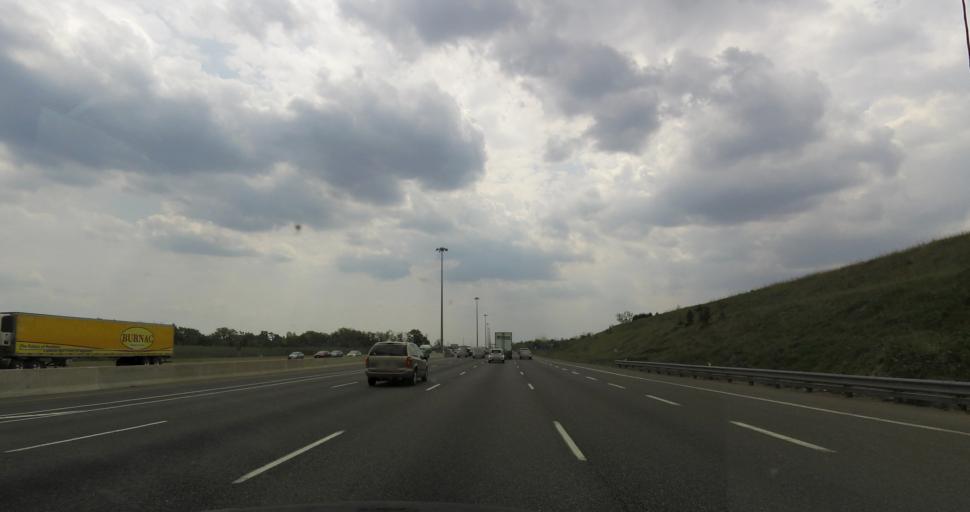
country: CA
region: Ontario
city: Oakville
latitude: 43.4070
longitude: -79.7439
